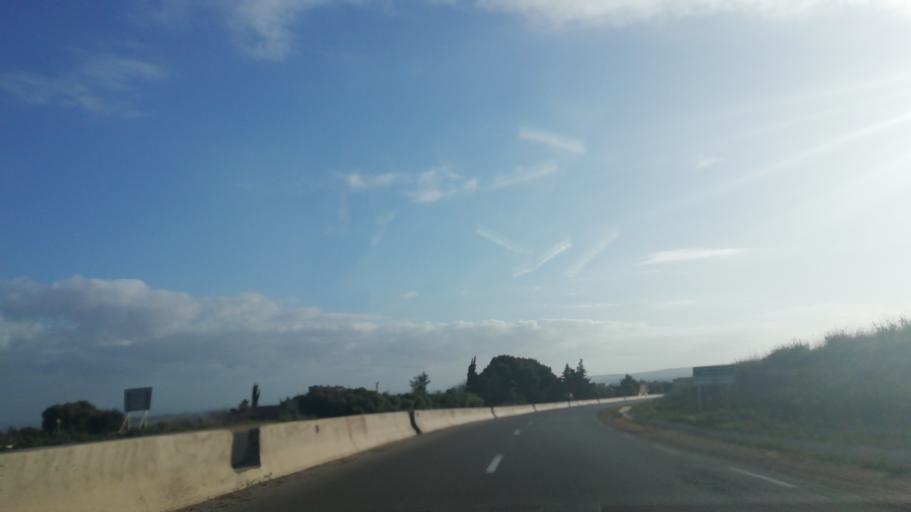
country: DZ
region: Mostaganem
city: Mostaganem
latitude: 36.1066
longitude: 0.2950
